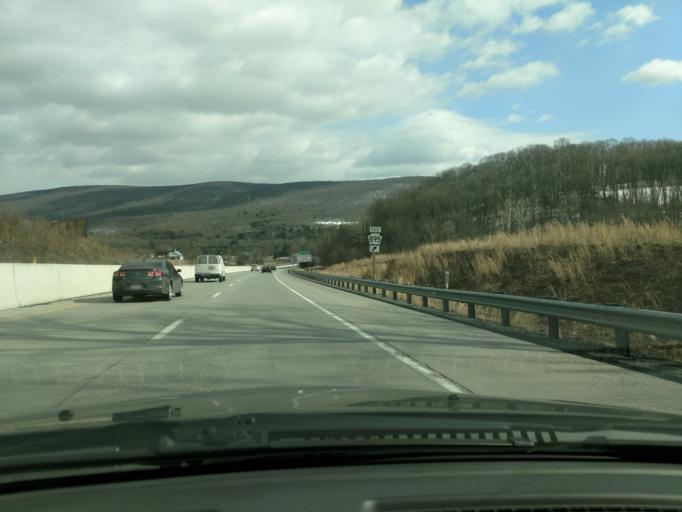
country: US
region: Pennsylvania
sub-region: Berks County
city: West Hamburg
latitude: 40.6137
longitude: -76.0371
